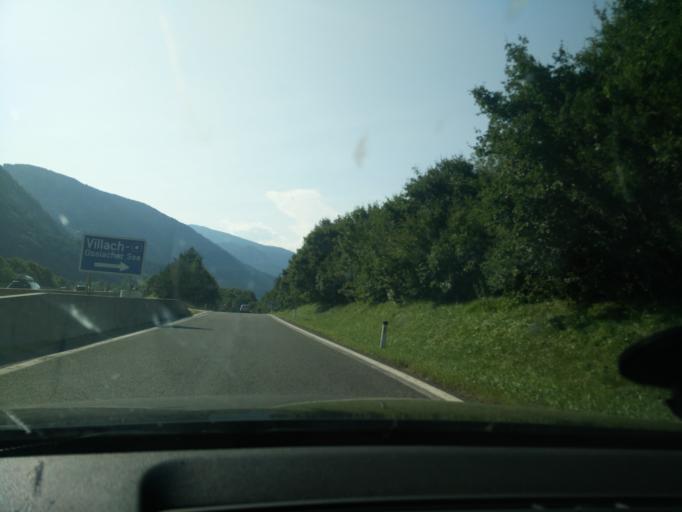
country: AT
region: Carinthia
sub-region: Villach Stadt
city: Villach
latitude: 46.6496
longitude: 13.8752
